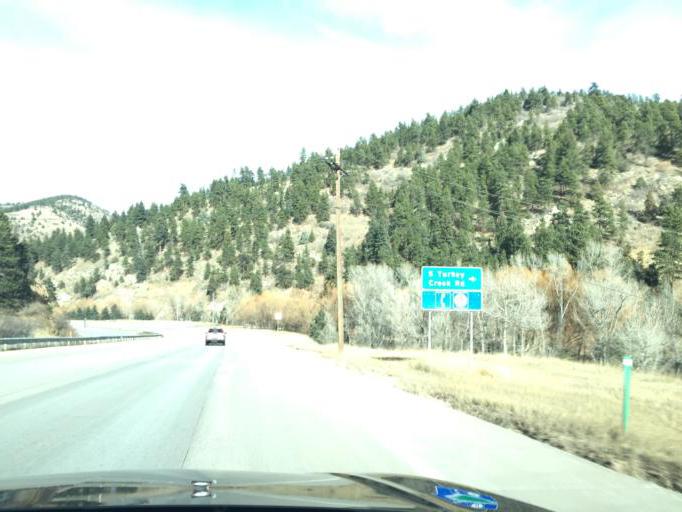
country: US
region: Colorado
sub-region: Jefferson County
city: Indian Hills
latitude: 39.6097
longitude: -105.2318
